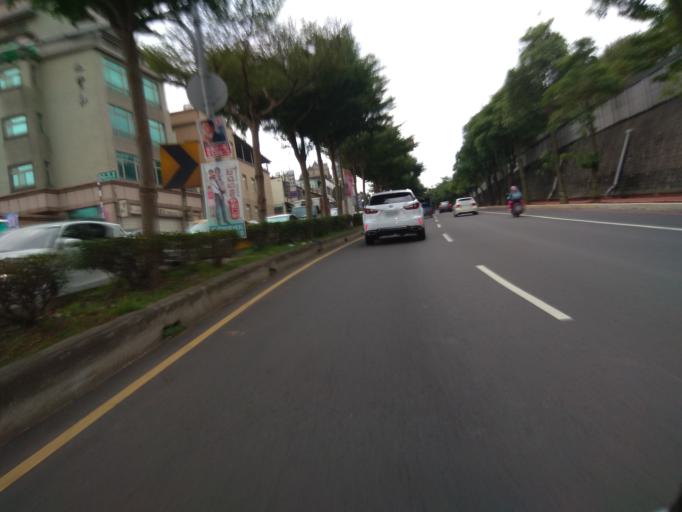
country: TW
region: Taiwan
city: Daxi
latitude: 24.9069
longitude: 121.2118
